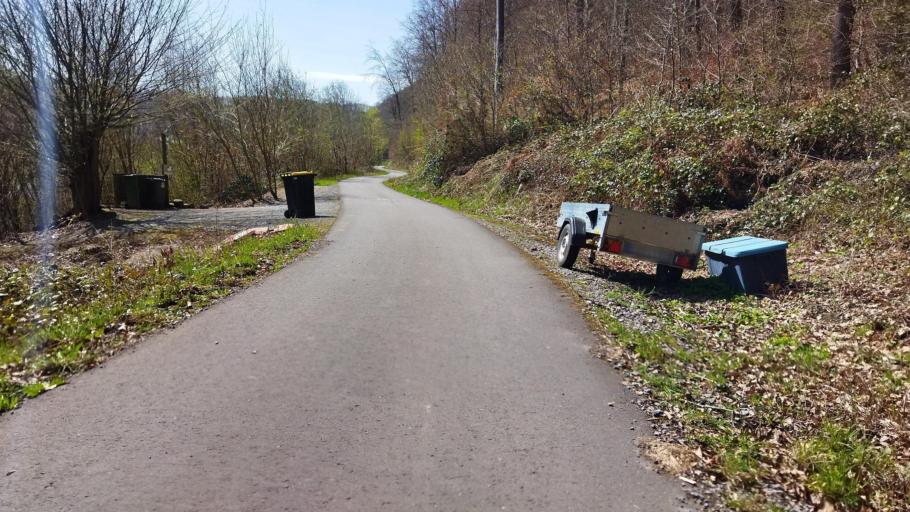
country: DE
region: Lower Saxony
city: Bad Karlshafen
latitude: 51.6529
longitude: 9.4614
